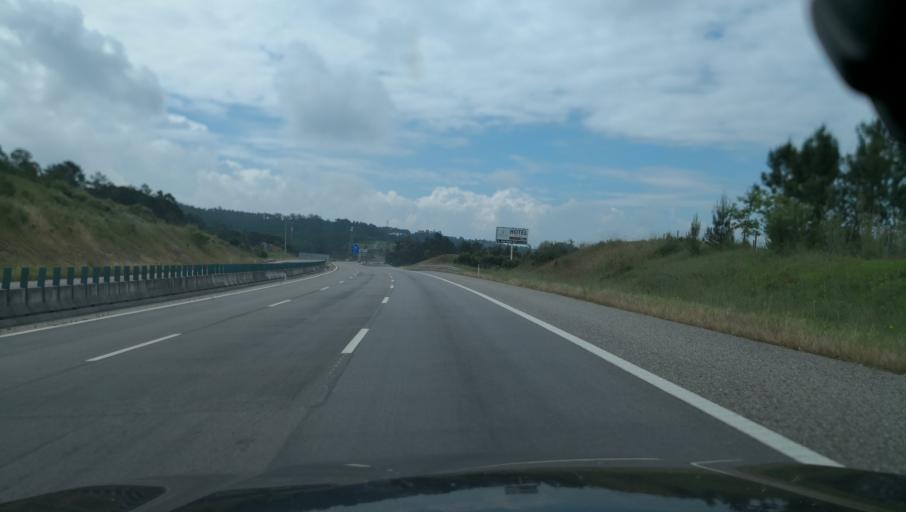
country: PT
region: Leiria
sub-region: Leiria
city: Souto da Carpalhosa
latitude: 39.8380
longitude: -8.8359
